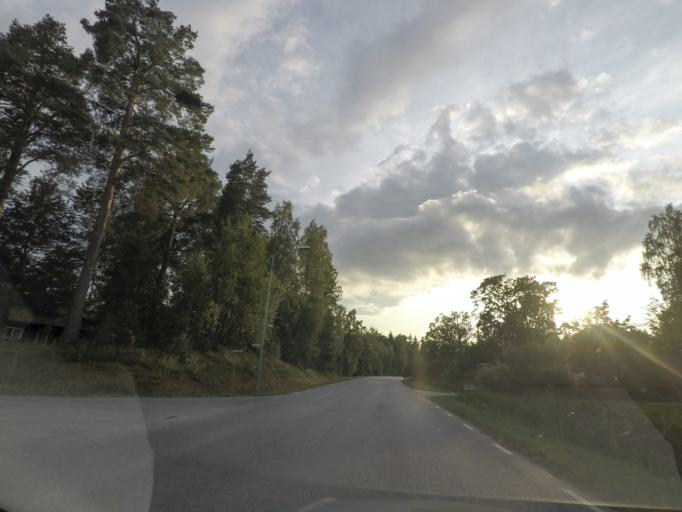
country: SE
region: OErebro
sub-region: Lindesbergs Kommun
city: Frovi
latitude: 59.4615
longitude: 15.3834
